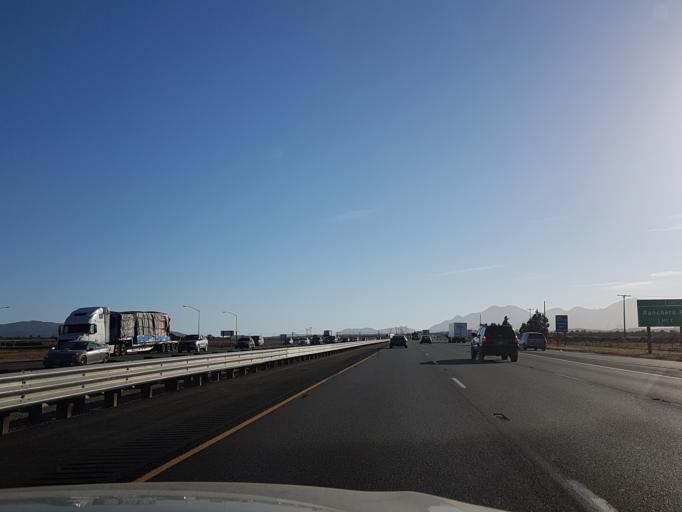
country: US
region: California
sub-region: San Bernardino County
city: Oak Hills
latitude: 34.3989
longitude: -117.4024
